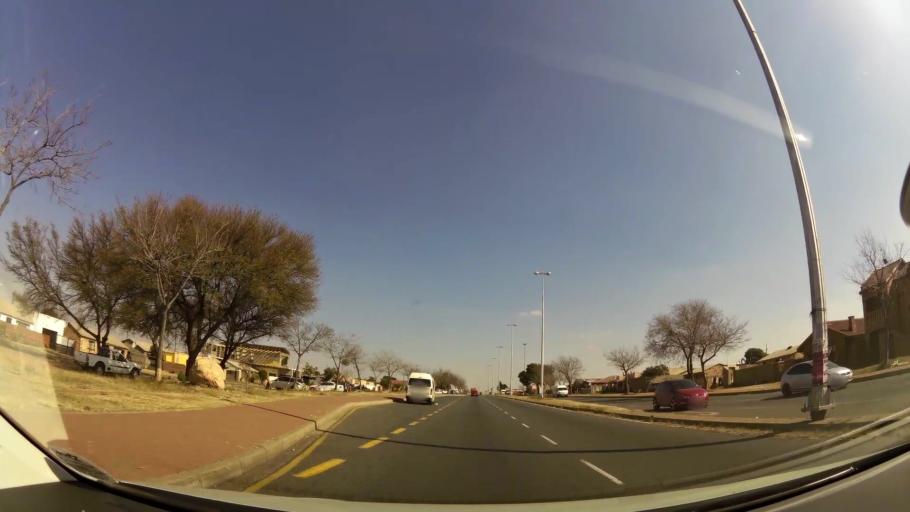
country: ZA
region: Gauteng
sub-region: City of Johannesburg Metropolitan Municipality
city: Soweto
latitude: -26.2768
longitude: 27.8670
